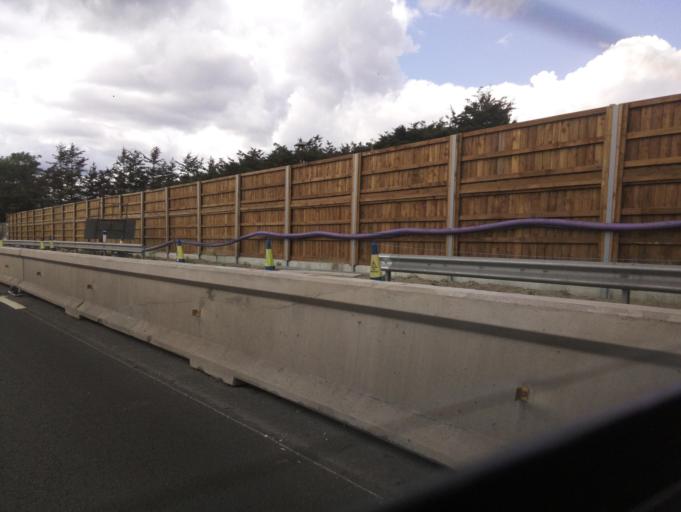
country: GB
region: England
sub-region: Surrey
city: Colnbrook
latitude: 51.4936
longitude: -0.5287
